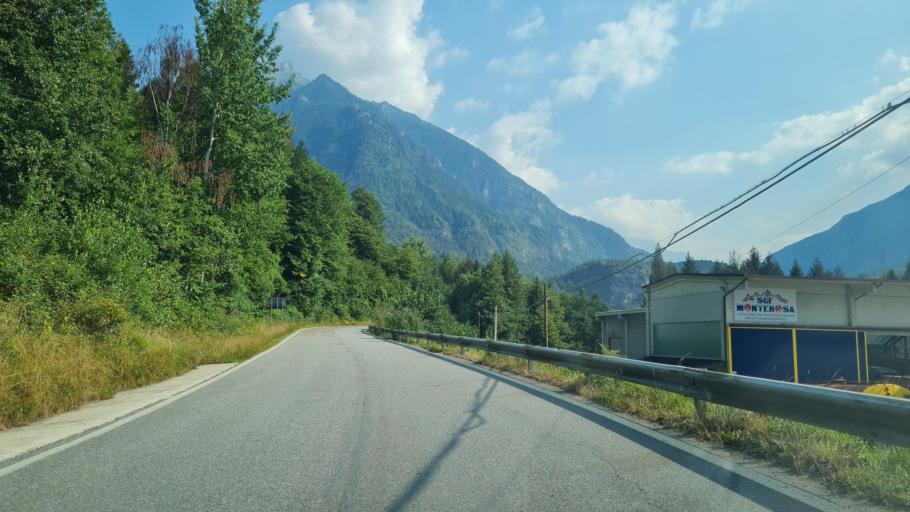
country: IT
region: Piedmont
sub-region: Provincia Verbano-Cusio-Ossola
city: Baceno
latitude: 46.2480
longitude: 8.3231
